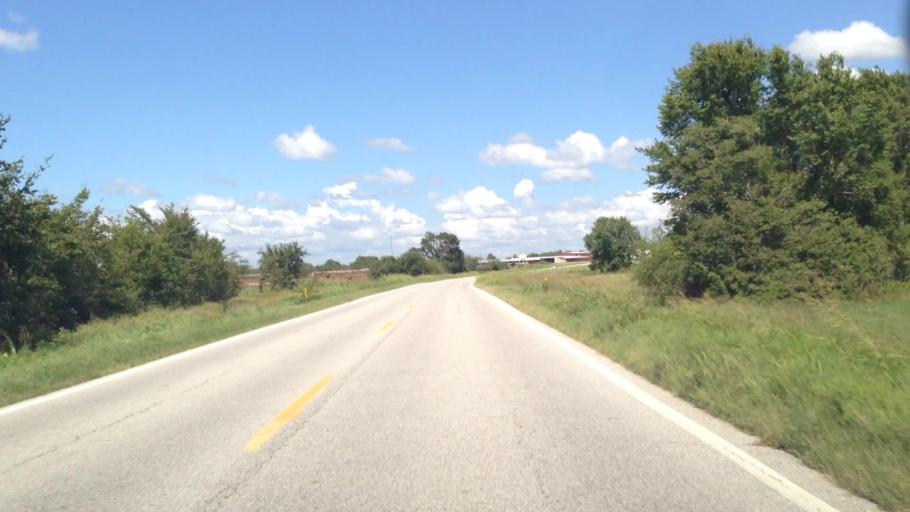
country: US
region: Kansas
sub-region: Labette County
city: Chetopa
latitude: 36.8595
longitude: -95.1153
